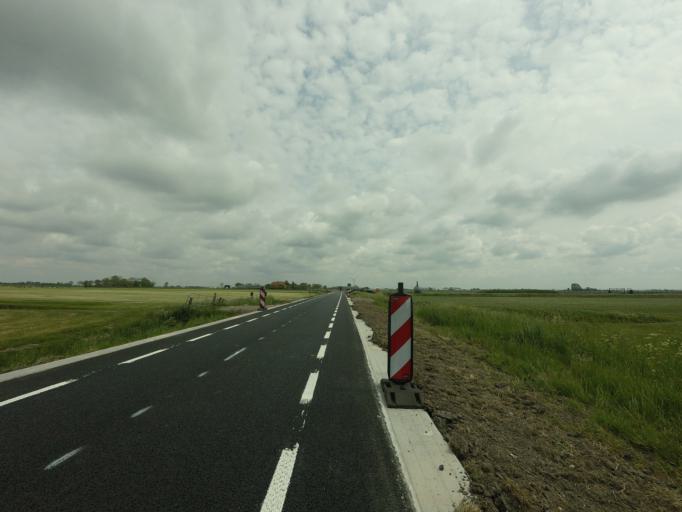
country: NL
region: Friesland
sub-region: Gemeente Littenseradiel
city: Wommels
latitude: 53.1056
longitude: 5.5463
